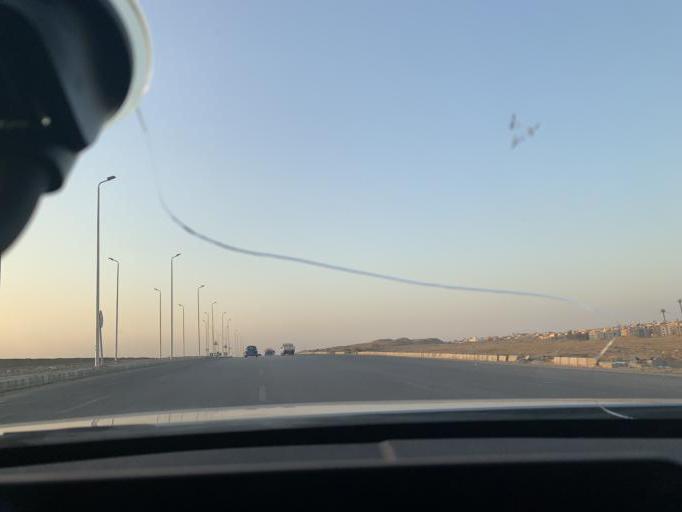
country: EG
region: Muhafazat al Qahirah
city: Halwan
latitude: 29.9867
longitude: 31.4688
